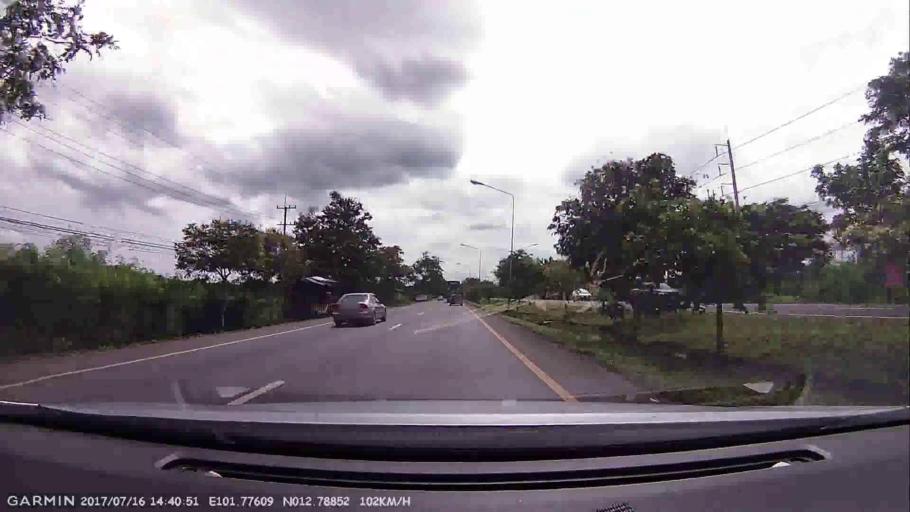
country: TH
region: Chanthaburi
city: Na Yai Am
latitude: 12.7885
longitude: 101.7758
